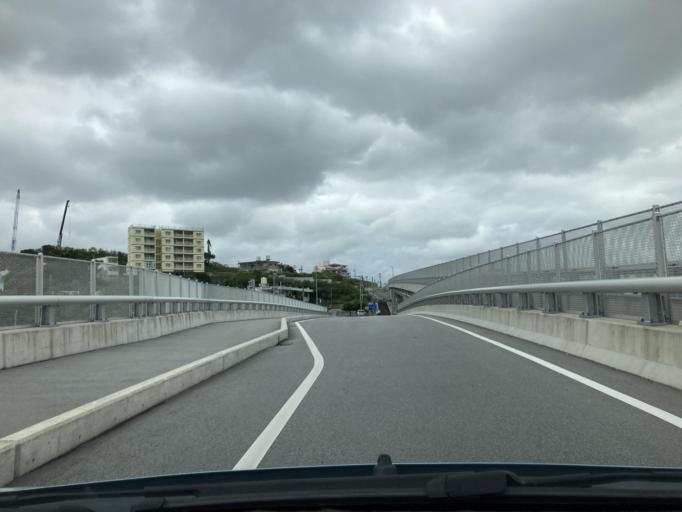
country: JP
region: Okinawa
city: Ginowan
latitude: 26.2415
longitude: 127.7415
